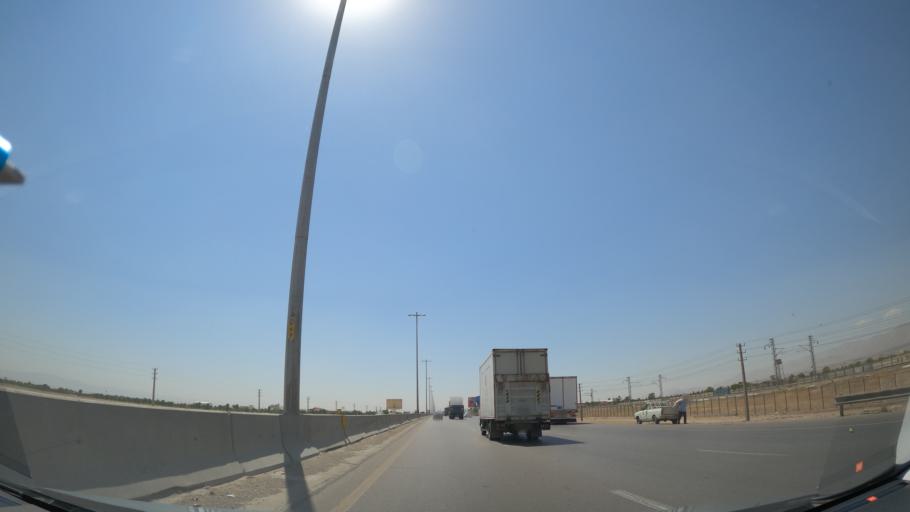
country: IR
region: Alborz
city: Hashtgerd
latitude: 35.9153
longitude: 50.8068
